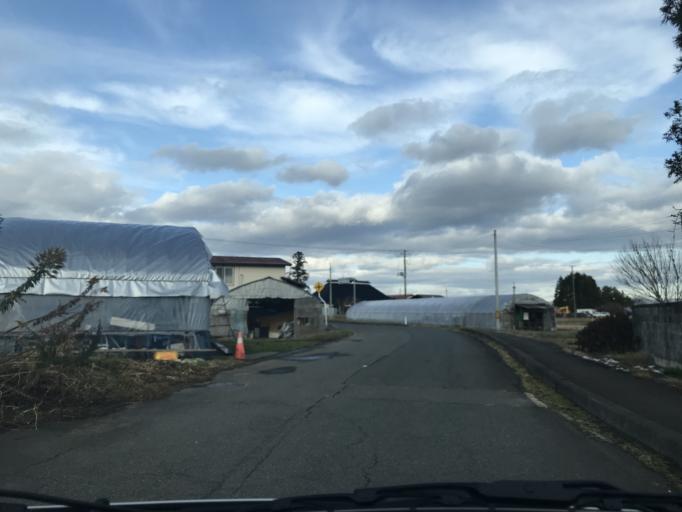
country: JP
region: Iwate
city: Mizusawa
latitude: 39.1864
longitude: 141.1025
